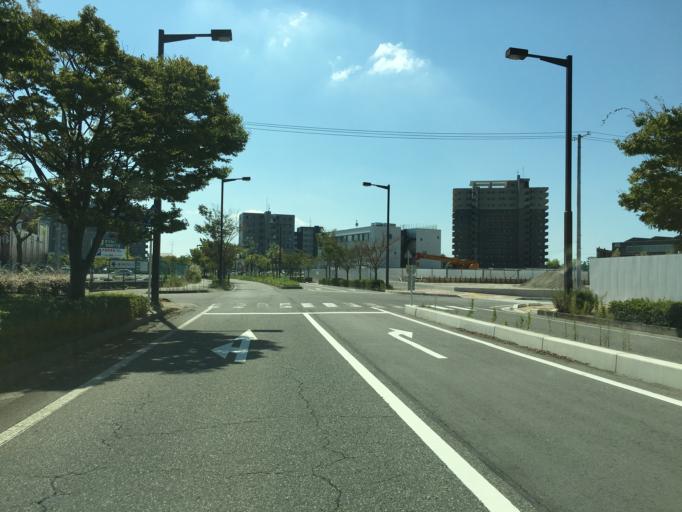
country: JP
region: Niigata
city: Niigata-shi
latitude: 37.8949
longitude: 139.0172
